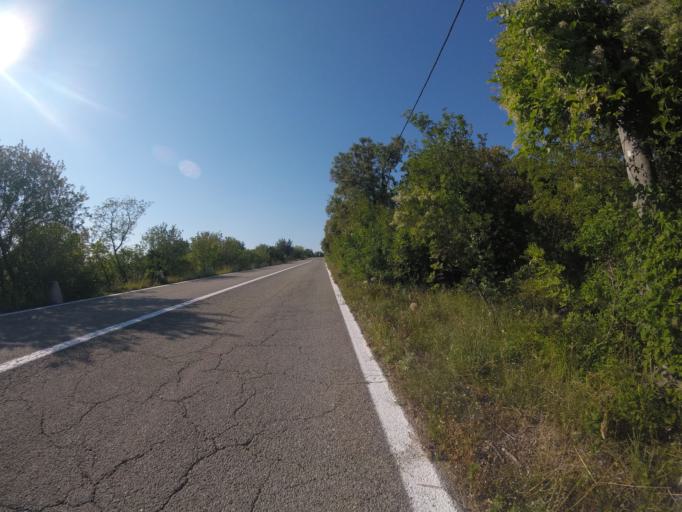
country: HR
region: Primorsko-Goranska
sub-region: Grad Crikvenica
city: Jadranovo
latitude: 45.2483
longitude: 14.6088
